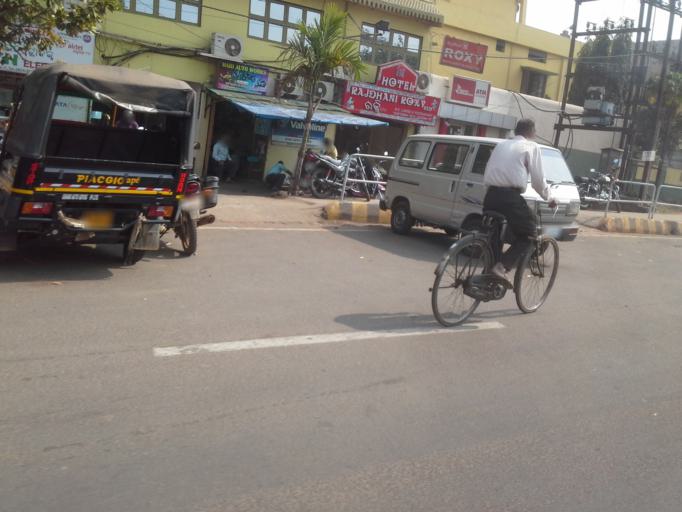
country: IN
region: Odisha
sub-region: Khordha
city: Bhubaneshwar
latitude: 20.2797
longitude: 85.8439
